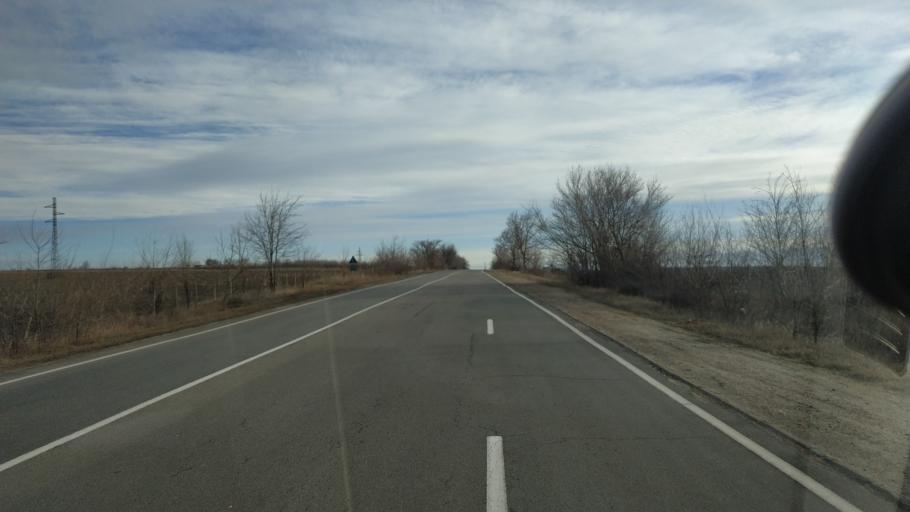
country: MD
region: Chisinau
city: Vadul lui Voda
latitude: 47.0753
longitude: 29.0247
